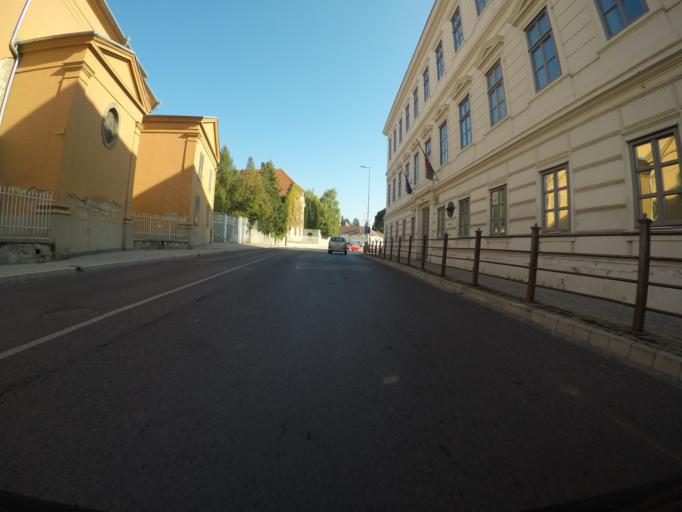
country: HU
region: Baranya
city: Pecs
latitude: 46.0792
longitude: 18.2355
